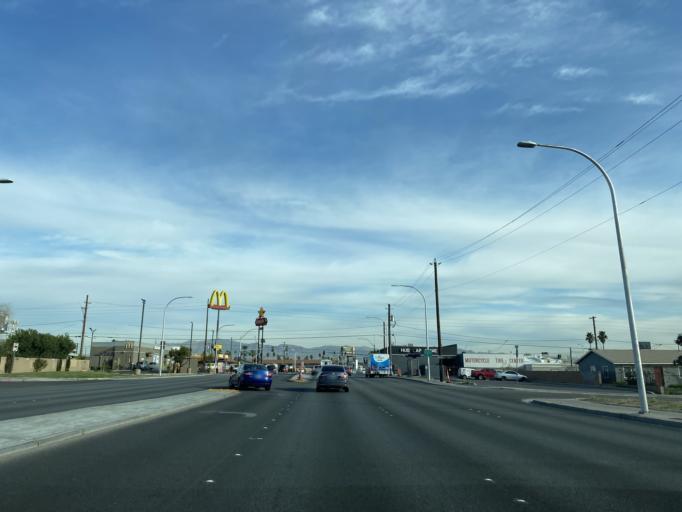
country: US
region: Nevada
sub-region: Clark County
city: Las Vegas
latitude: 36.1573
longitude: -115.1188
